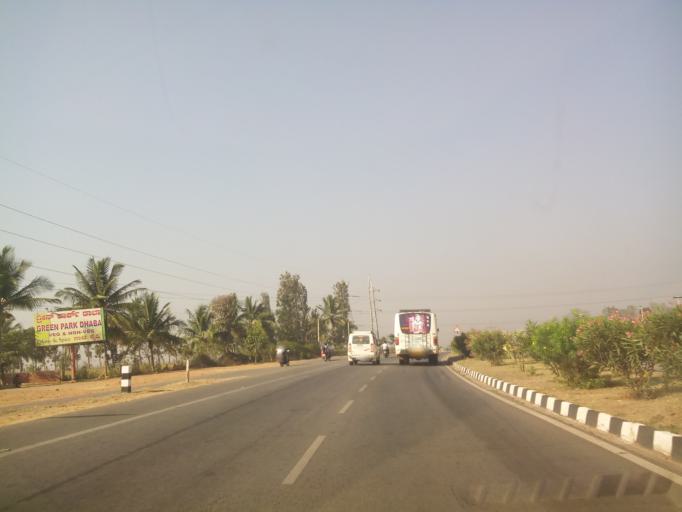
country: IN
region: Karnataka
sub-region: Bangalore Rural
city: Nelamangala
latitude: 13.0837
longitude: 77.3733
